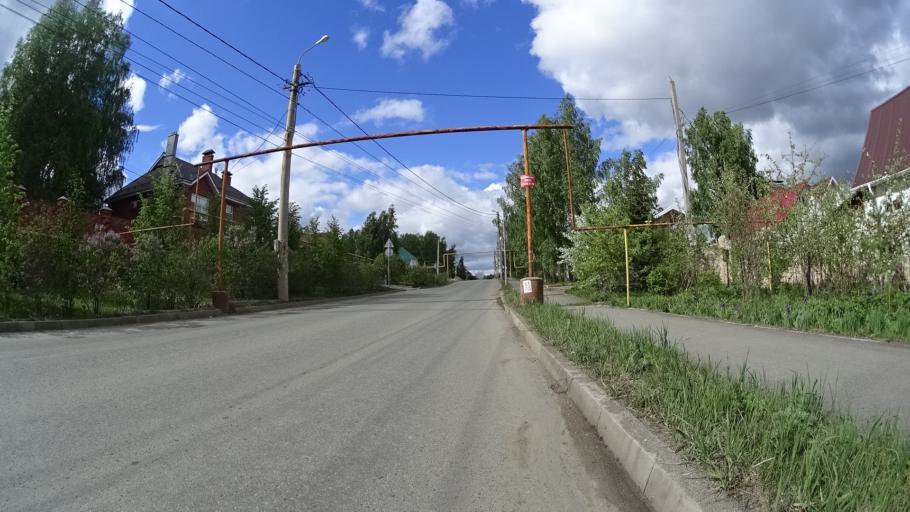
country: RU
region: Chelyabinsk
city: Sargazy
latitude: 55.1566
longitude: 61.2520
